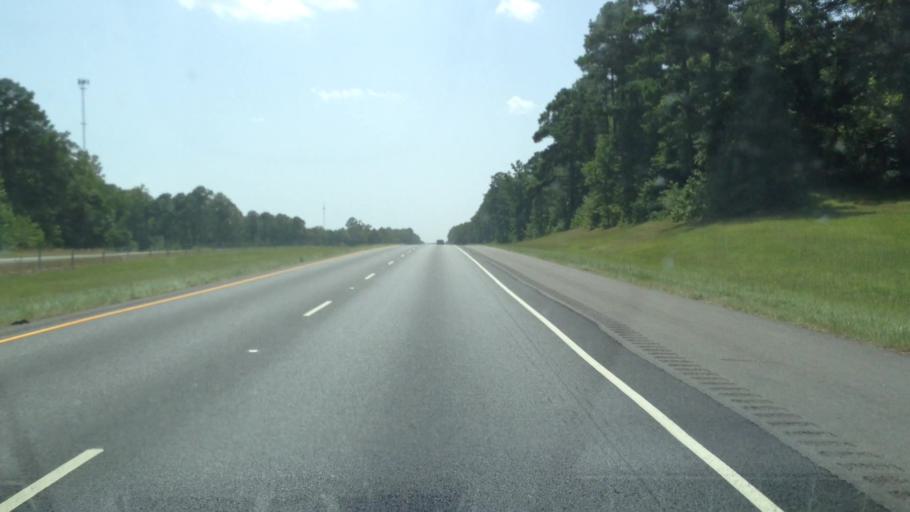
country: US
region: Louisiana
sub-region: Webster Parish
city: Minden
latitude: 32.5630
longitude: -93.1083
